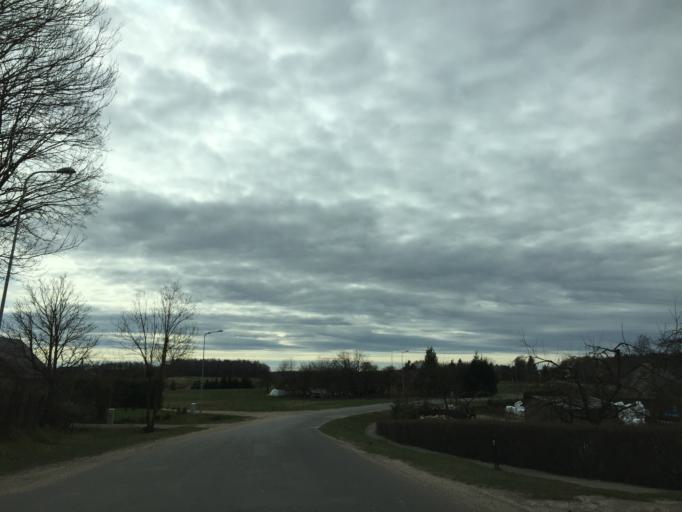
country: LT
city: Silale
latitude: 55.6206
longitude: 22.2260
